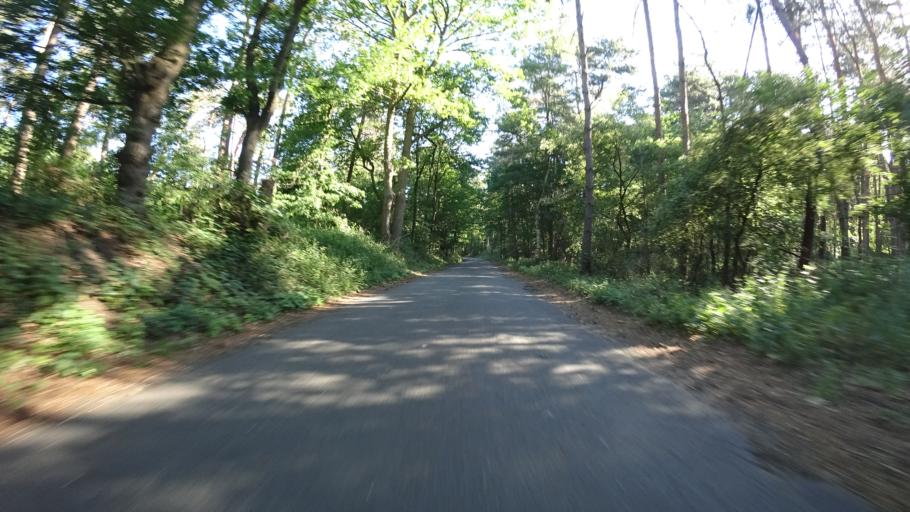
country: DE
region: North Rhine-Westphalia
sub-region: Regierungsbezirk Detmold
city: Rheda-Wiedenbruck
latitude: 51.8777
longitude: 8.3153
